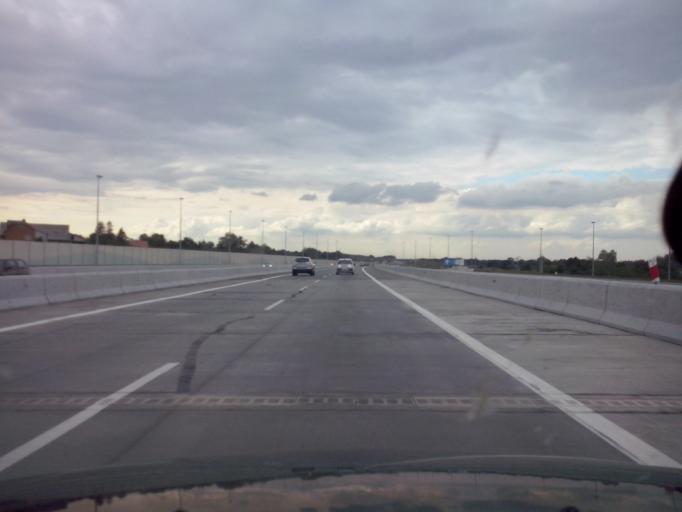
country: PL
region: Lesser Poland Voivodeship
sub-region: Powiat wielicki
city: Podleze
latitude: 50.0039
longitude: 20.1755
